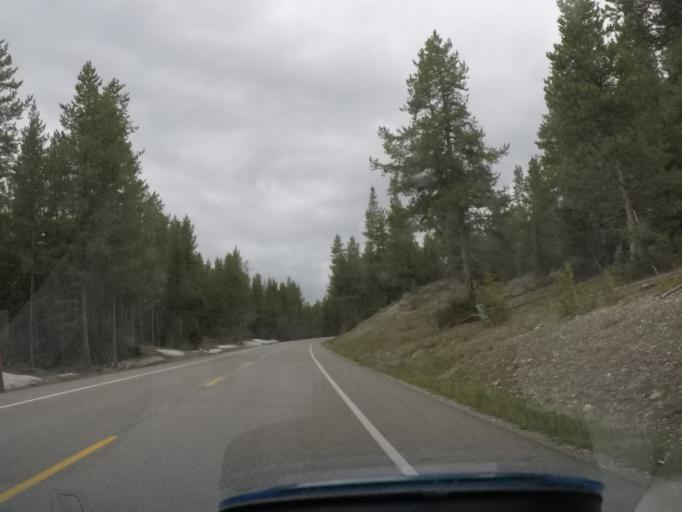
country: US
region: Wyoming
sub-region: Teton County
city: Moose Wilson Road
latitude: 43.9153
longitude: -110.6341
